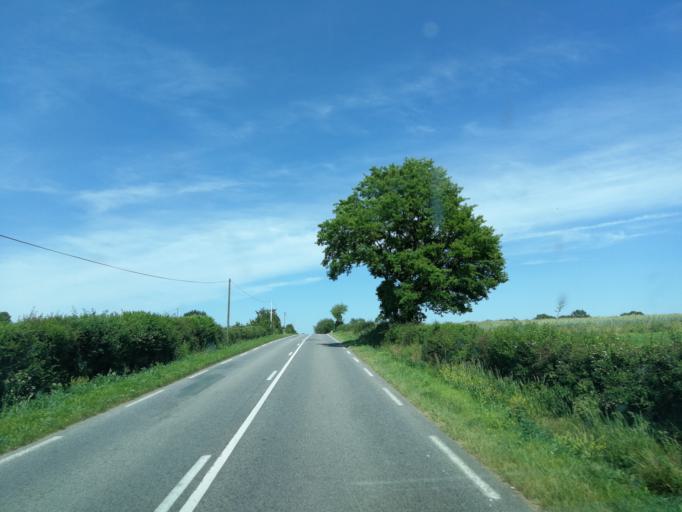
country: FR
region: Poitou-Charentes
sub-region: Departement des Deux-Sevres
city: Saint-Varent
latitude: 46.8849
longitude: -0.3156
